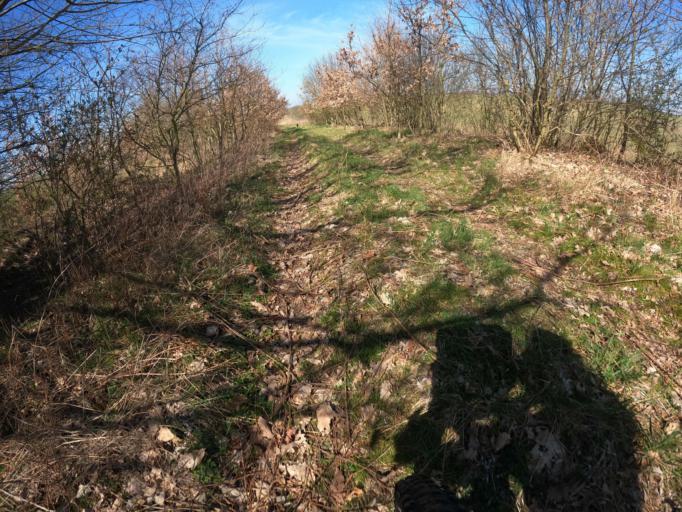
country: PL
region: West Pomeranian Voivodeship
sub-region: Powiat gryficki
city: Brojce
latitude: 53.9808
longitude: 15.3903
